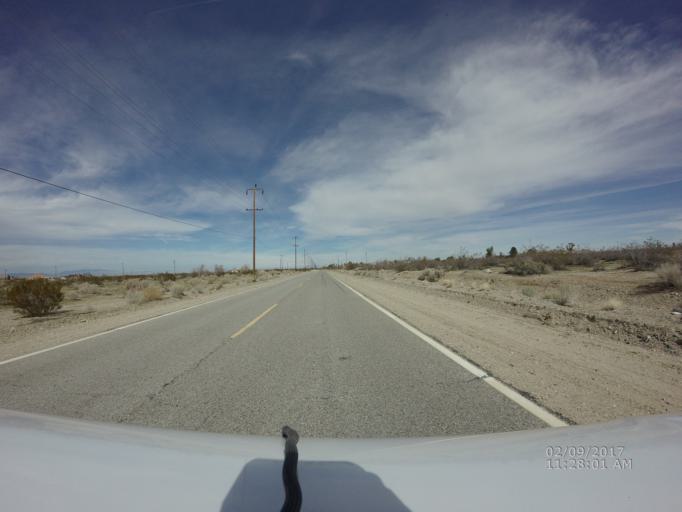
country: US
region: California
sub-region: Los Angeles County
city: Littlerock
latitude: 34.5412
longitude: -117.9229
